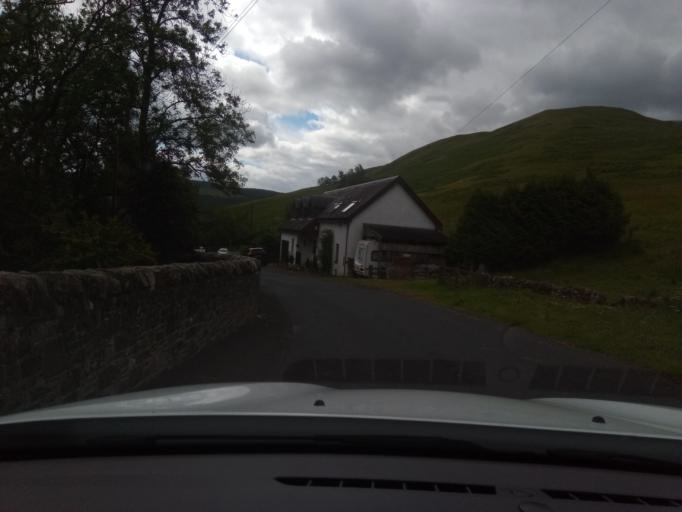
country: GB
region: Scotland
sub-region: The Scottish Borders
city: Innerleithen
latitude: 55.4486
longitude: -3.1033
